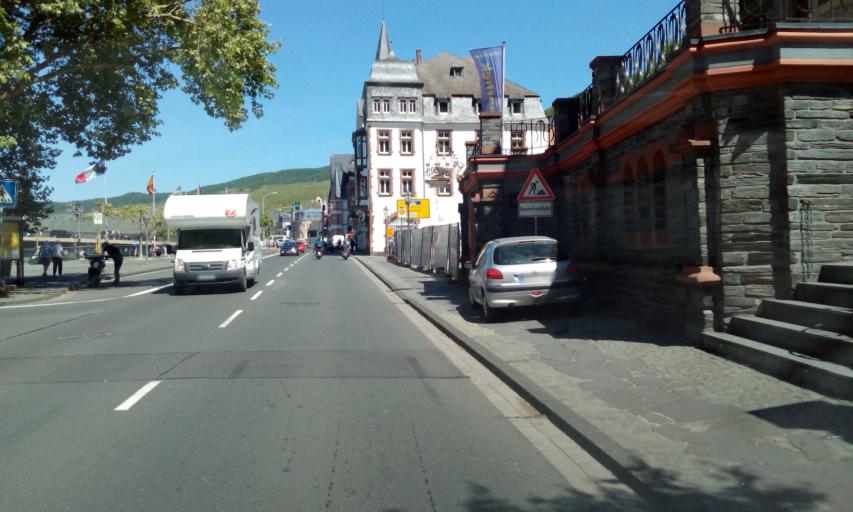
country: DE
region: Rheinland-Pfalz
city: Bernkastel-Kues
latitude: 49.9144
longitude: 7.0748
